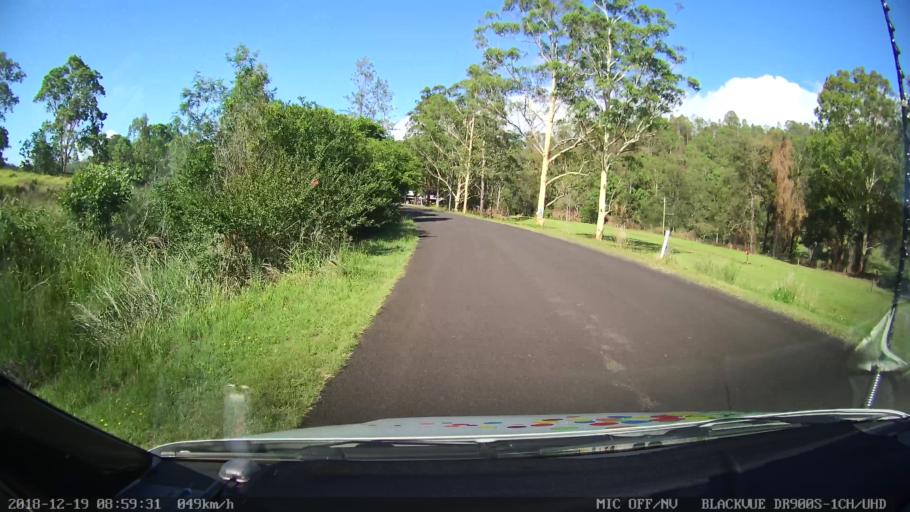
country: AU
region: New South Wales
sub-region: Kyogle
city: Kyogle
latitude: -28.4274
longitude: 152.9591
